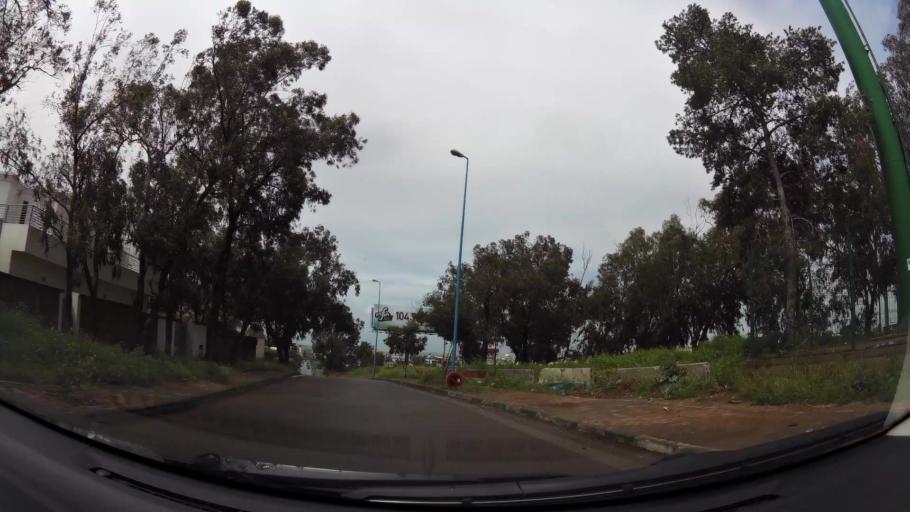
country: MA
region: Grand Casablanca
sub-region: Casablanca
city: Casablanca
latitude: 33.5309
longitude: -7.6384
